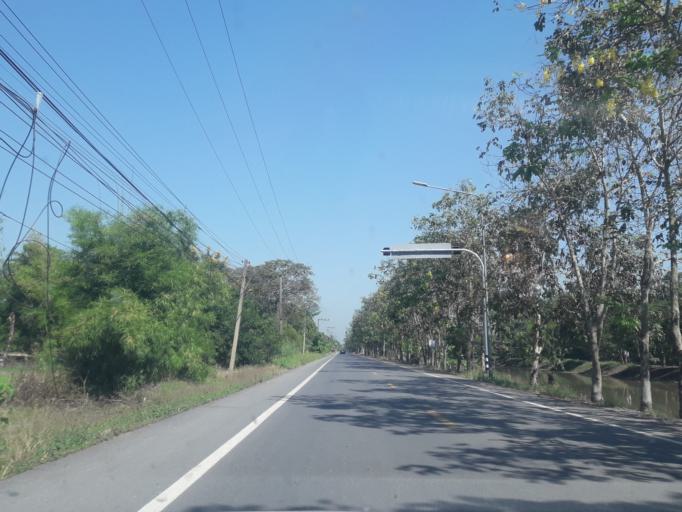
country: TH
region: Pathum Thani
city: Nong Suea
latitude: 14.1696
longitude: 100.8458
